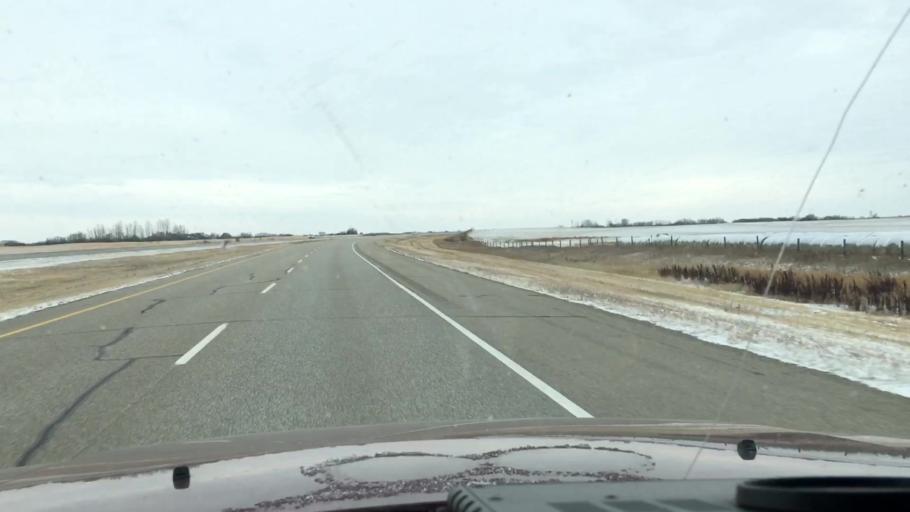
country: CA
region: Saskatchewan
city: Watrous
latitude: 51.3651
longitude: -106.1303
